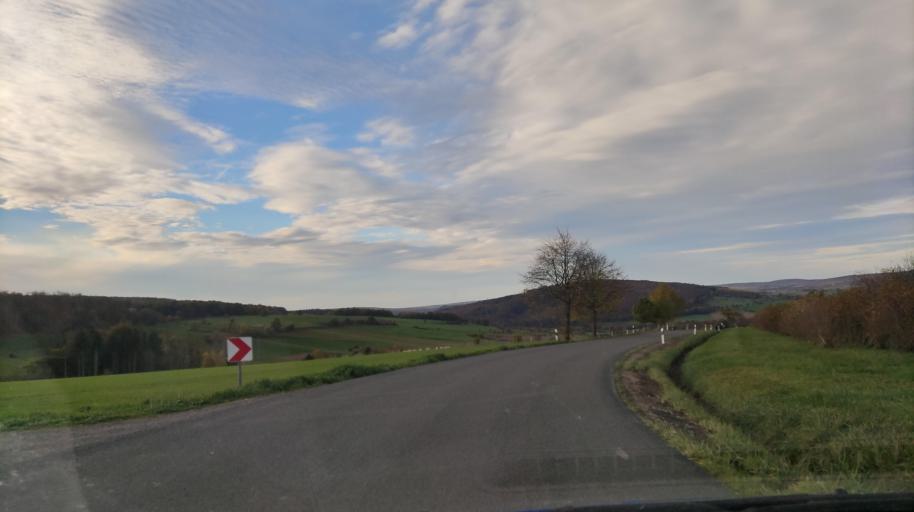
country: DE
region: Lower Saxony
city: Uslar
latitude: 51.6077
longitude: 9.6308
